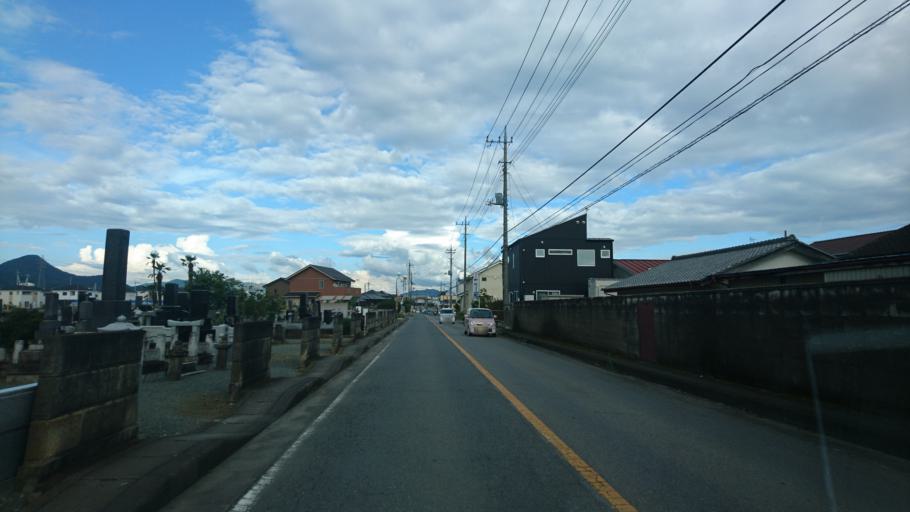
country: JP
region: Gunma
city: Omamacho-omama
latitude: 36.4094
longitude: 139.2874
